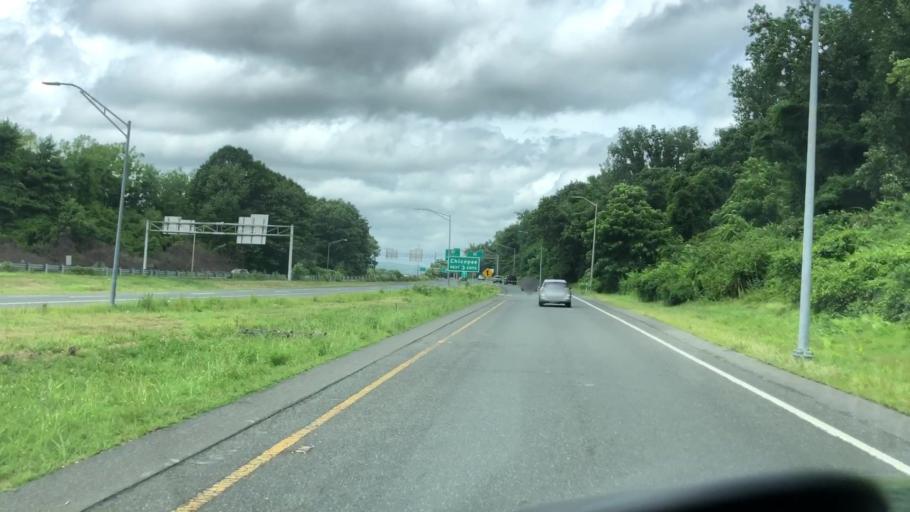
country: US
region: Massachusetts
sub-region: Hampden County
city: Chicopee
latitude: 42.1356
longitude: -72.6086
